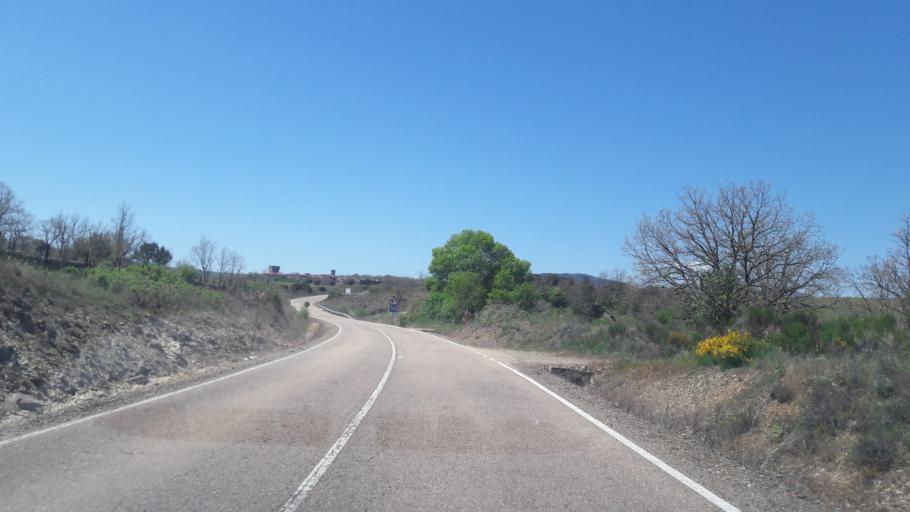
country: ES
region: Castille and Leon
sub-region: Provincia de Salamanca
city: Monleon
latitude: 40.5906
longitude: -5.8347
